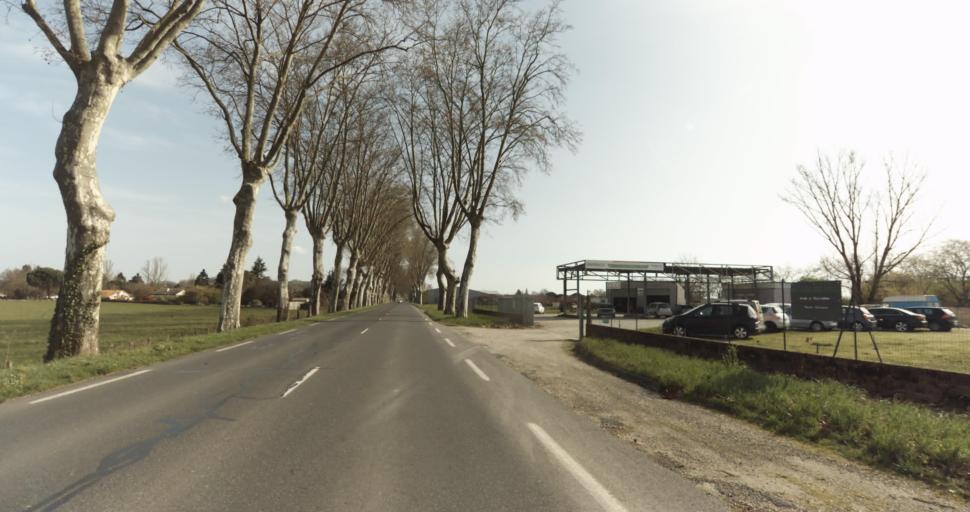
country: FR
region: Midi-Pyrenees
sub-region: Departement du Tarn
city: Saint-Sulpice-la-Pointe
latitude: 43.7763
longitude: 1.6659
